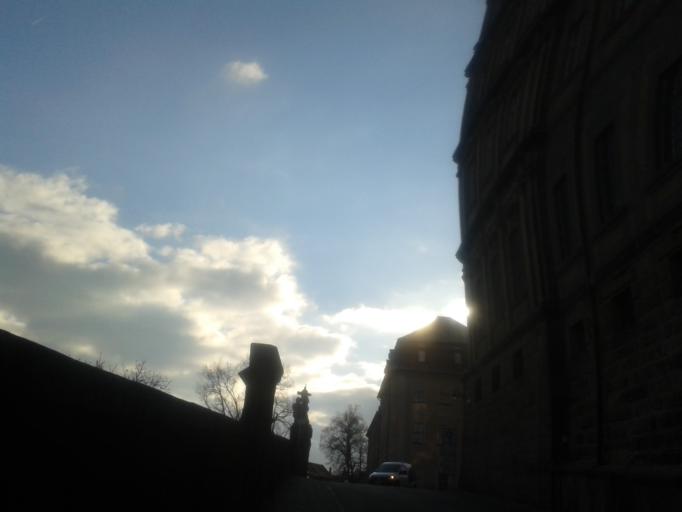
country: DE
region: Bavaria
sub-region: Upper Franconia
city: Bamberg
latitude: 49.8918
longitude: 10.8830
